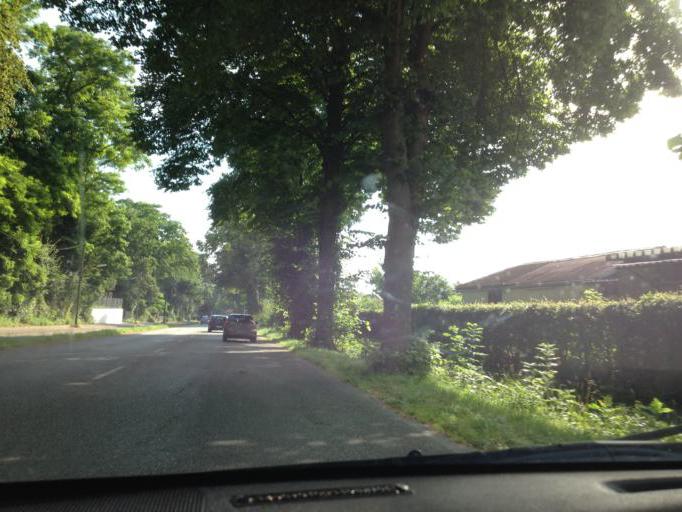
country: DE
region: North Rhine-Westphalia
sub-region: Regierungsbezirk Arnsberg
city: Dortmund
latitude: 51.4796
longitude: 7.5011
